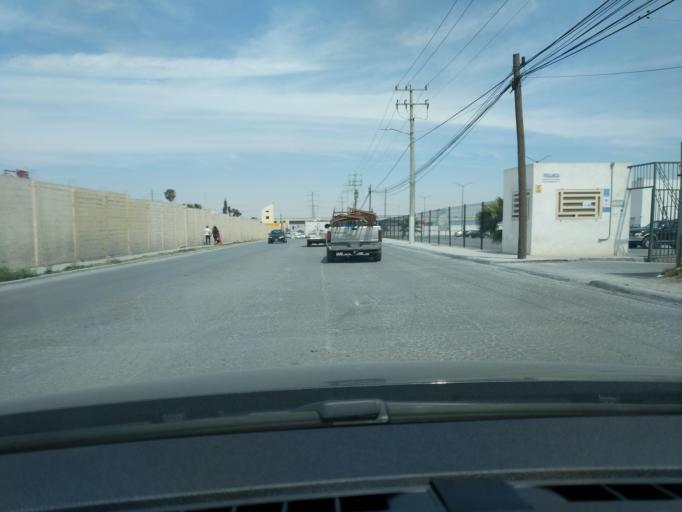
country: MX
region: Coahuila
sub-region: Arteaga
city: Arteaga
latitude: 25.4335
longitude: -100.9135
